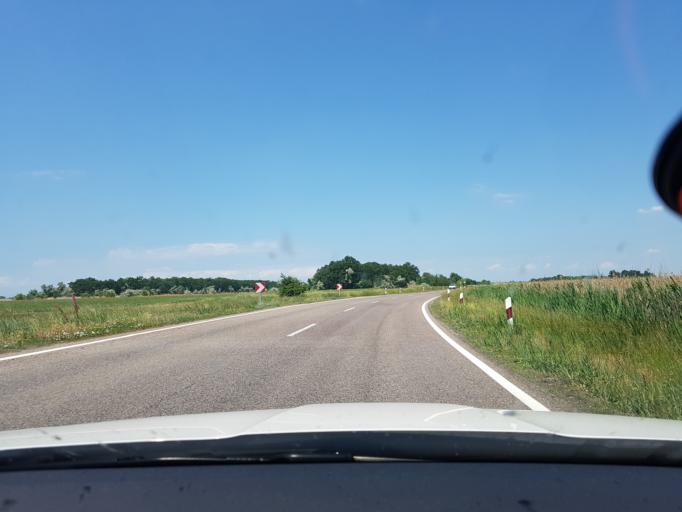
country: HU
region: Hajdu-Bihar
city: Egyek
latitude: 47.5599
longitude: 20.8642
